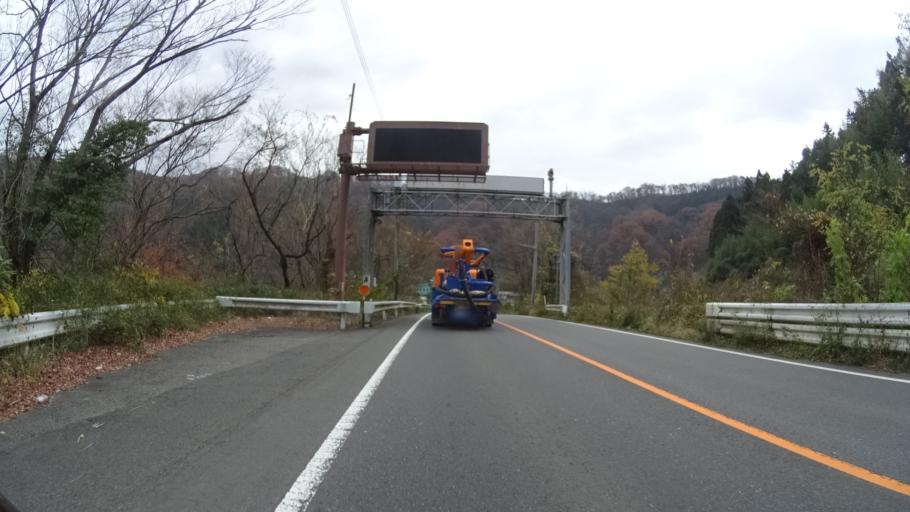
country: JP
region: Gunma
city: Numata
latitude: 36.5873
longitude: 139.0553
